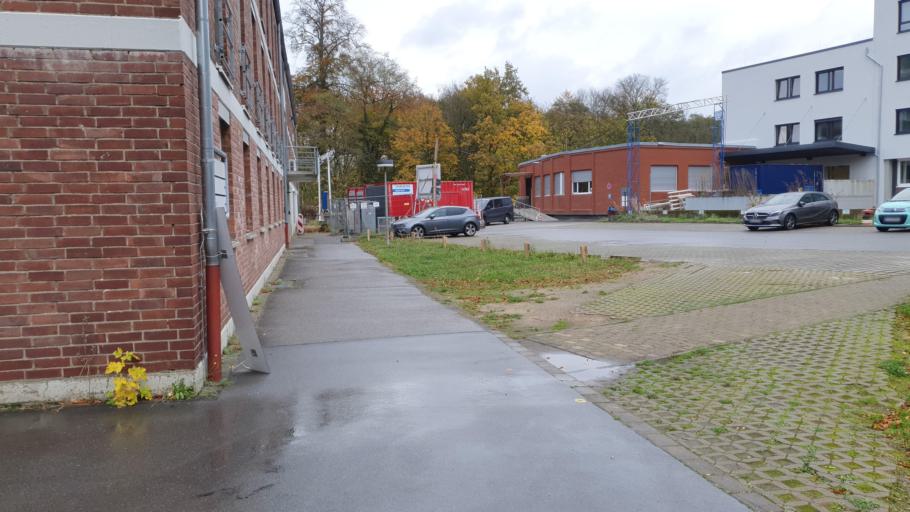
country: DE
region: North Rhine-Westphalia
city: Opladen
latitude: 51.0325
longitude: 7.0315
